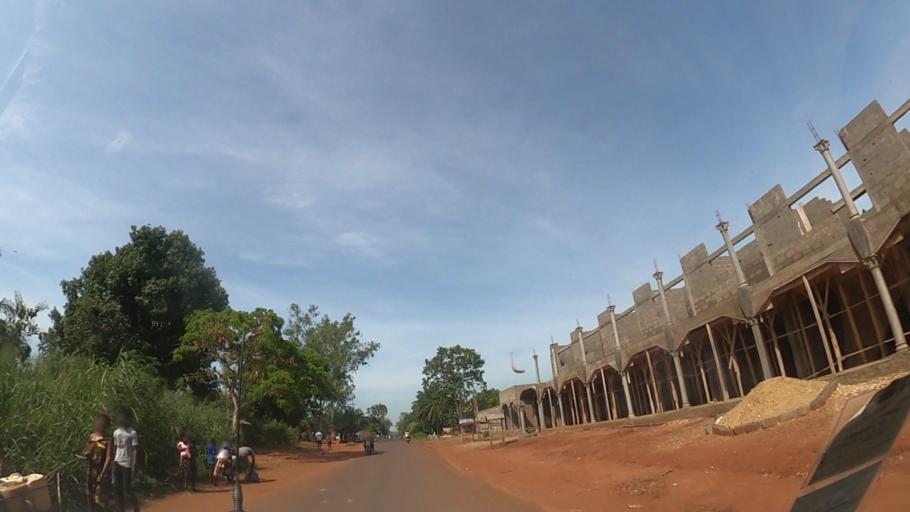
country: CF
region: Bangui
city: Bangui
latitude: 4.3143
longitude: 18.4909
